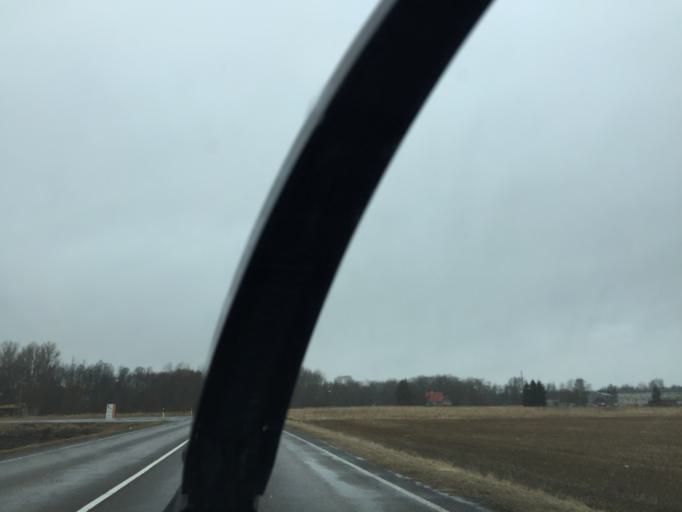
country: EE
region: Laeaene
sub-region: Ridala Parish
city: Uuemoisa
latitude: 58.8627
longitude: 23.6262
